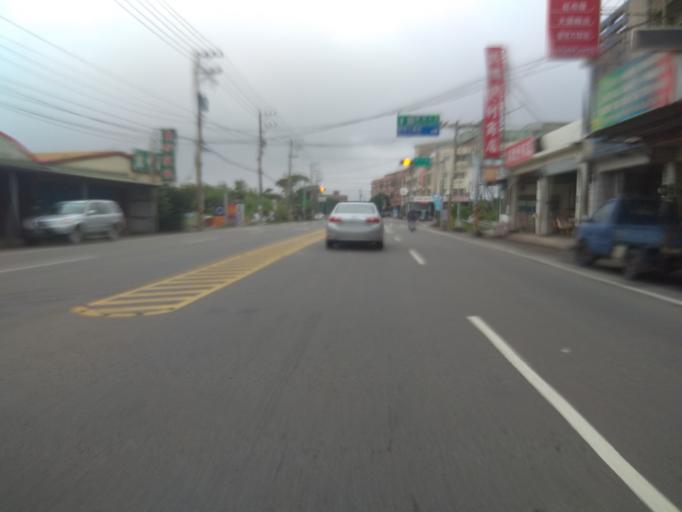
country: TW
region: Taiwan
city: Taoyuan City
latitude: 25.0303
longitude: 121.1050
